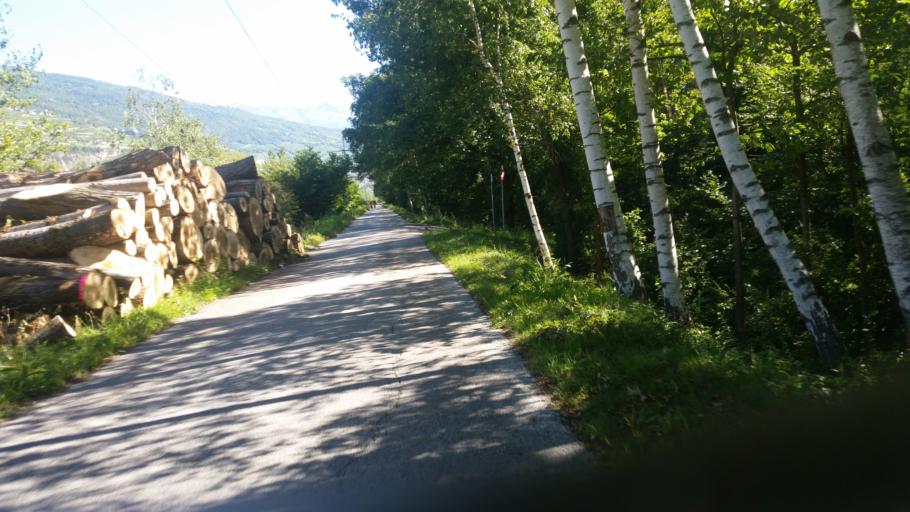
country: CH
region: Valais
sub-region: Sierre District
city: Grone
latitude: 46.2530
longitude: 7.4405
